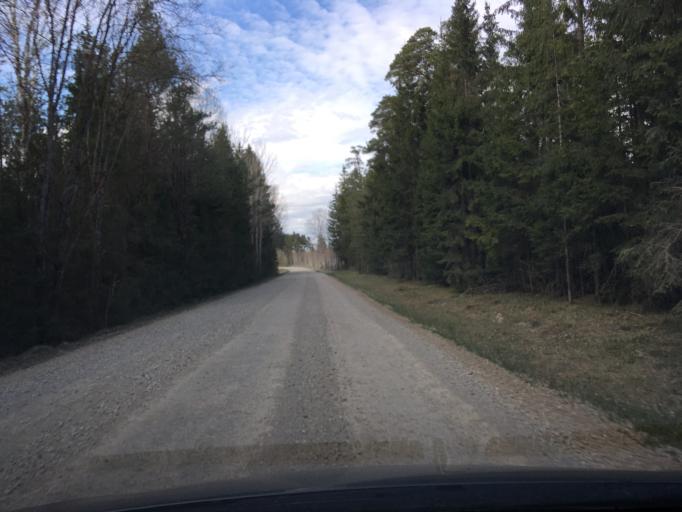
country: EE
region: Raplamaa
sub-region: Maerjamaa vald
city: Marjamaa
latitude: 58.9515
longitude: 24.3233
